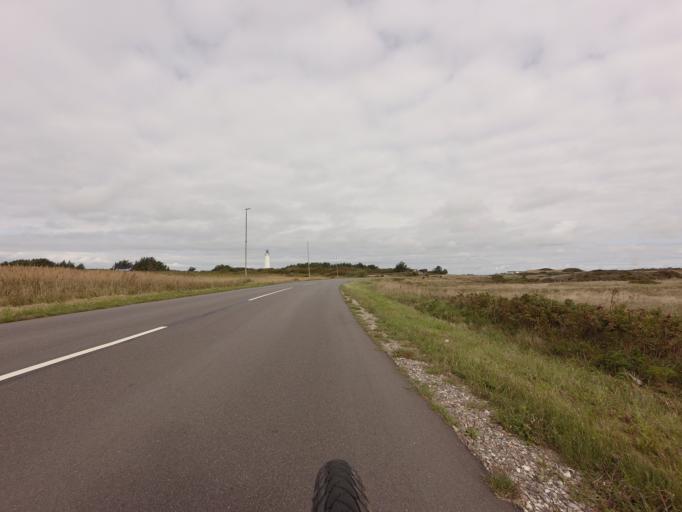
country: DK
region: North Denmark
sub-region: Hjorring Kommune
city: Hirtshals
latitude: 57.5813
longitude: 9.9440
